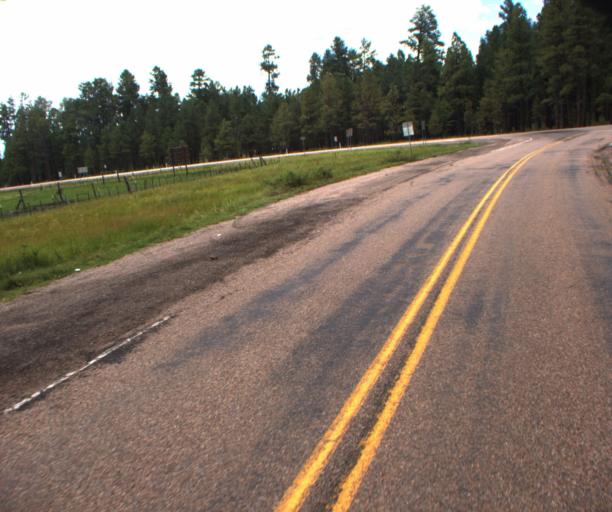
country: US
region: Arizona
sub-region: Navajo County
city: Pinetop-Lakeside
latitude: 34.0514
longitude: -109.7296
